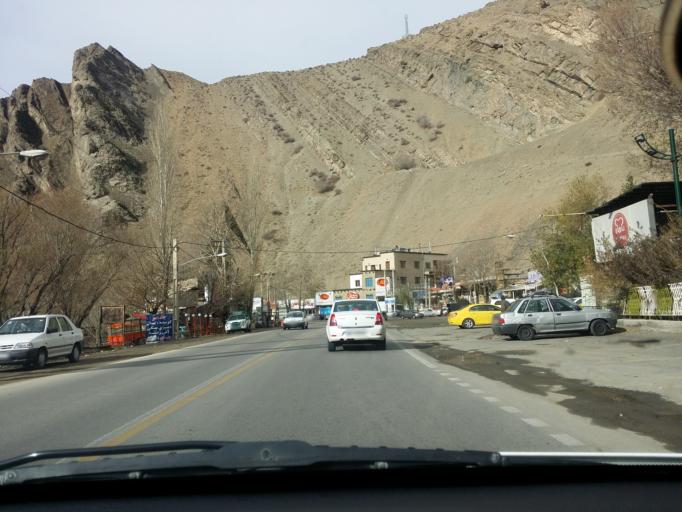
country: IR
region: Tehran
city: Tajrish
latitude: 36.0314
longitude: 51.2312
